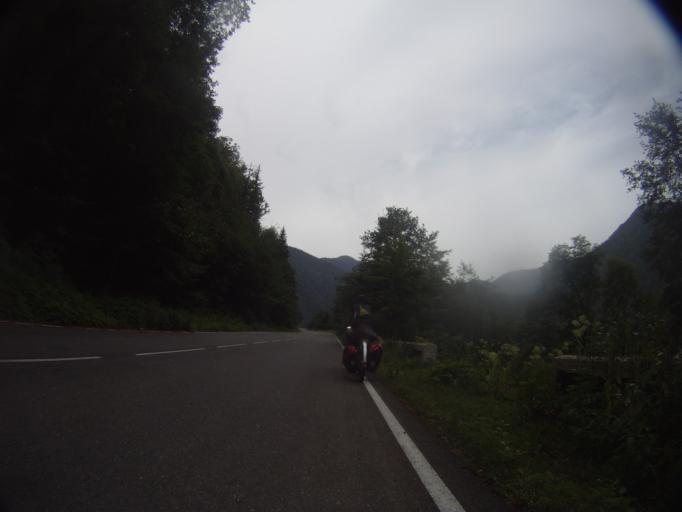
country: GE
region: Samegrelo and Zemo Svaneti
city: Jvari
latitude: 42.8342
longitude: 42.0225
